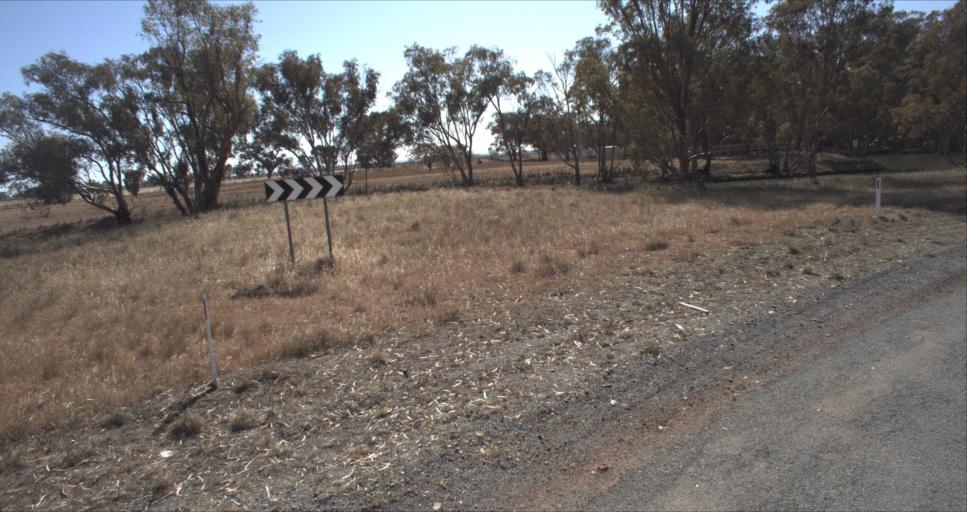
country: AU
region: New South Wales
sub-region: Leeton
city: Leeton
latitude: -34.6046
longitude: 146.2639
